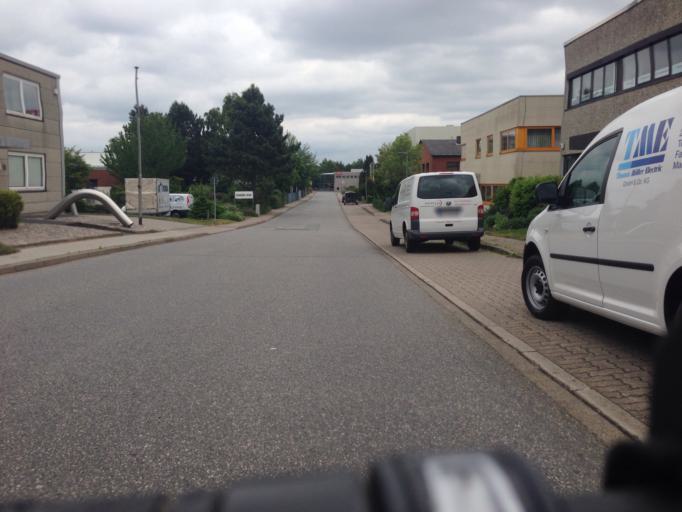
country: DE
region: Schleswig-Holstein
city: Barsbuettel
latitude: 53.5736
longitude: 10.1906
